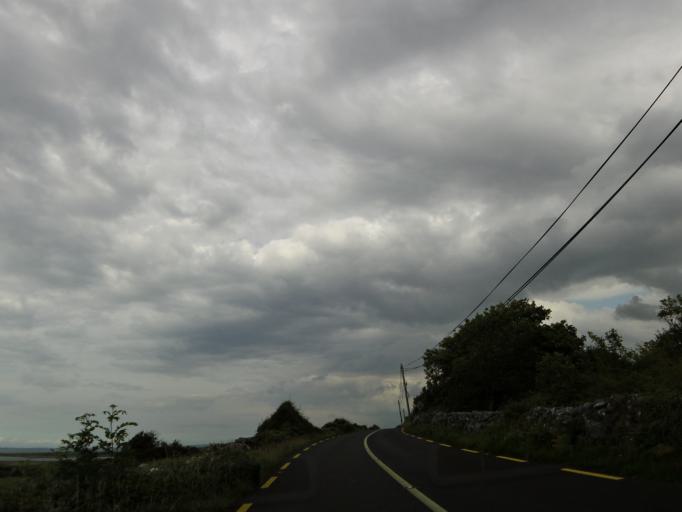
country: IE
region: Connaught
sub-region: County Galway
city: Bearna
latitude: 53.1287
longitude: -9.1217
